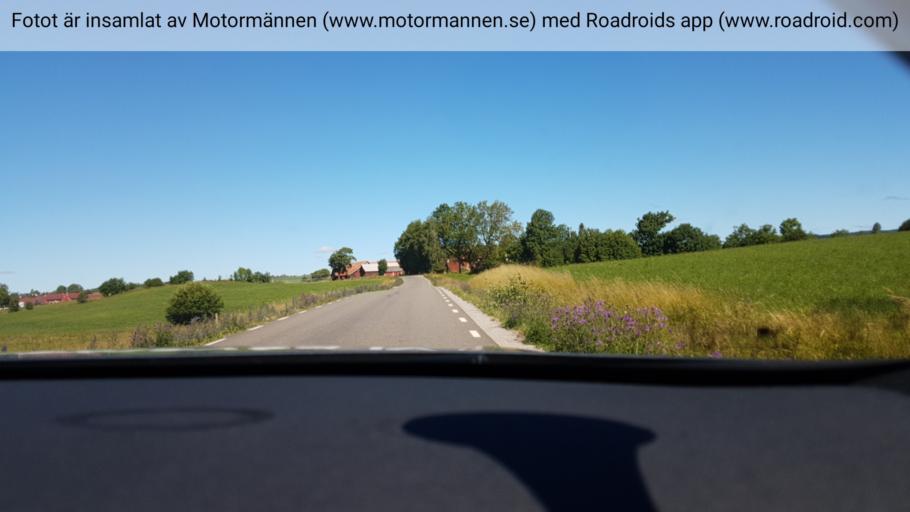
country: SE
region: Vaestra Goetaland
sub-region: Falkopings Kommun
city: Akarp
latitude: 58.2522
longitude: 13.6933
